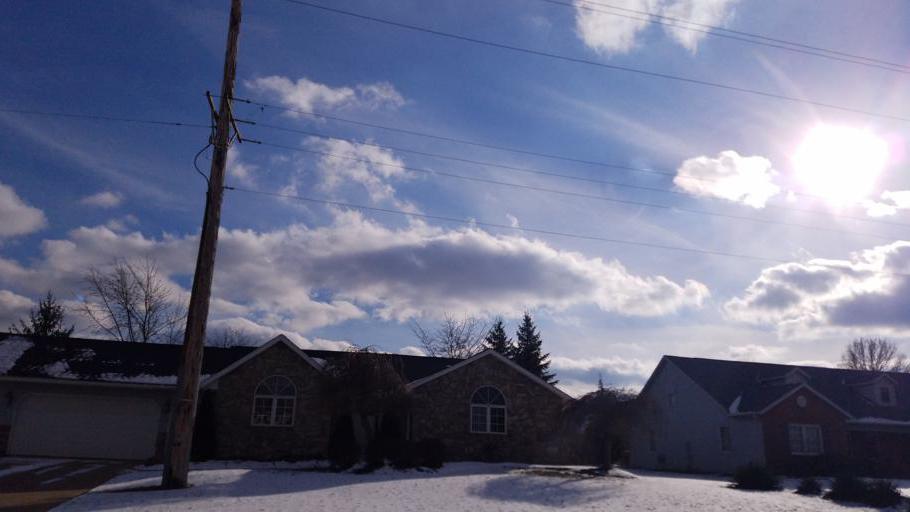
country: US
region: Ohio
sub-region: Richland County
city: Ontario
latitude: 40.7798
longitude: -82.6007
